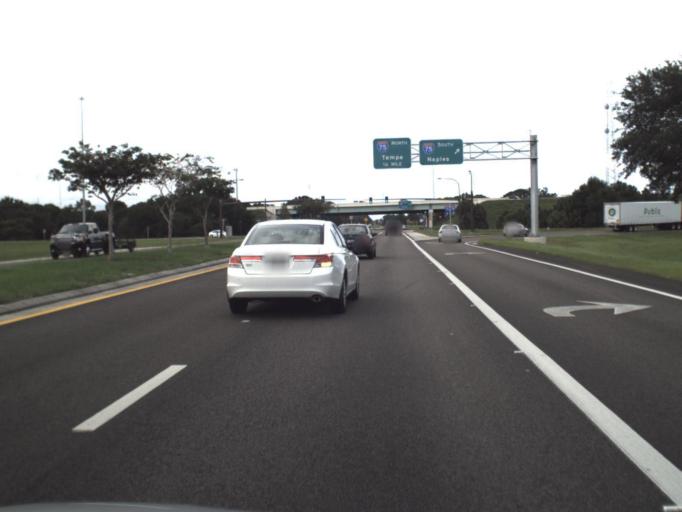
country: US
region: Florida
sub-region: Sarasota County
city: Plantation
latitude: 27.1084
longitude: -82.3843
